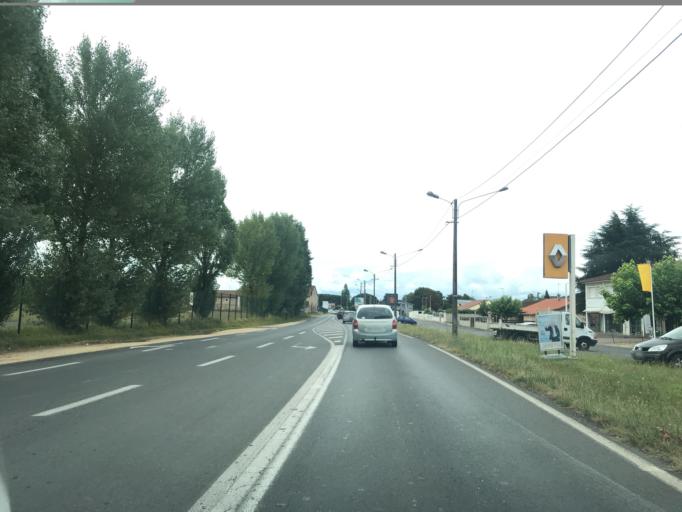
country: FR
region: Aquitaine
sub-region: Departement de la Dordogne
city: Chancelade
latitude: 45.1998
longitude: 0.6664
